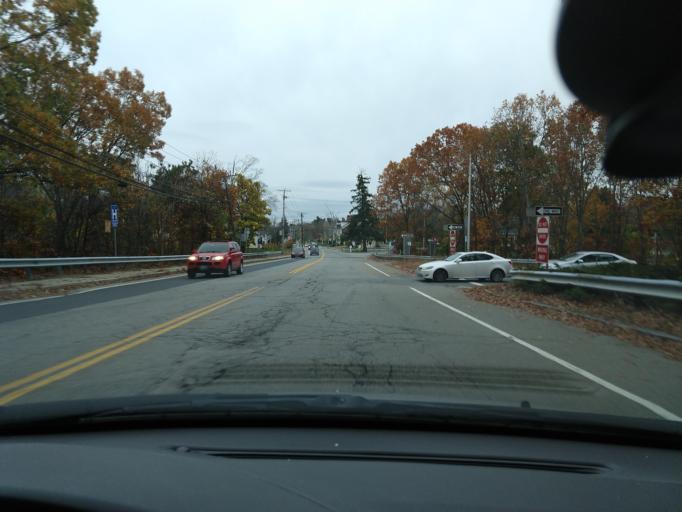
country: US
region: Massachusetts
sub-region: Middlesex County
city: Chelmsford
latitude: 42.6025
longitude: -71.3539
